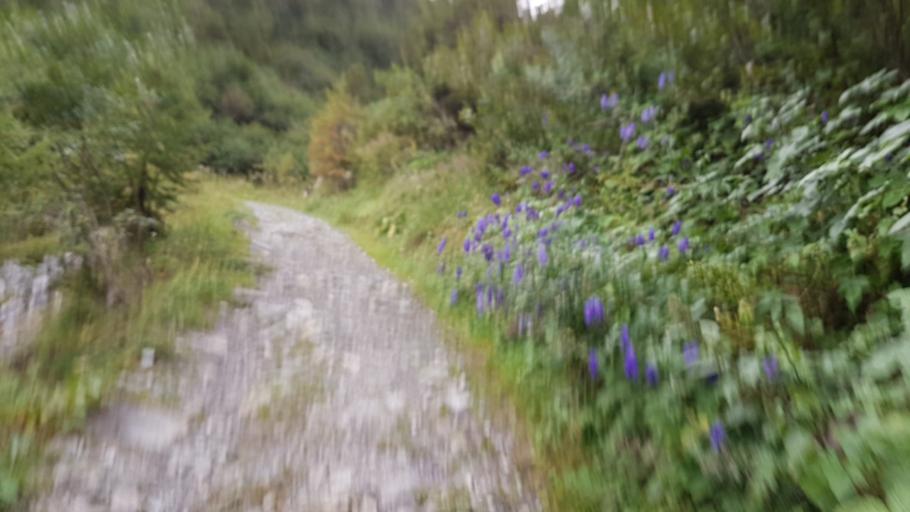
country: CH
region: Bern
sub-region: Frutigen-Niedersimmental District
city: Kandersteg
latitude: 46.4651
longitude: 7.6531
